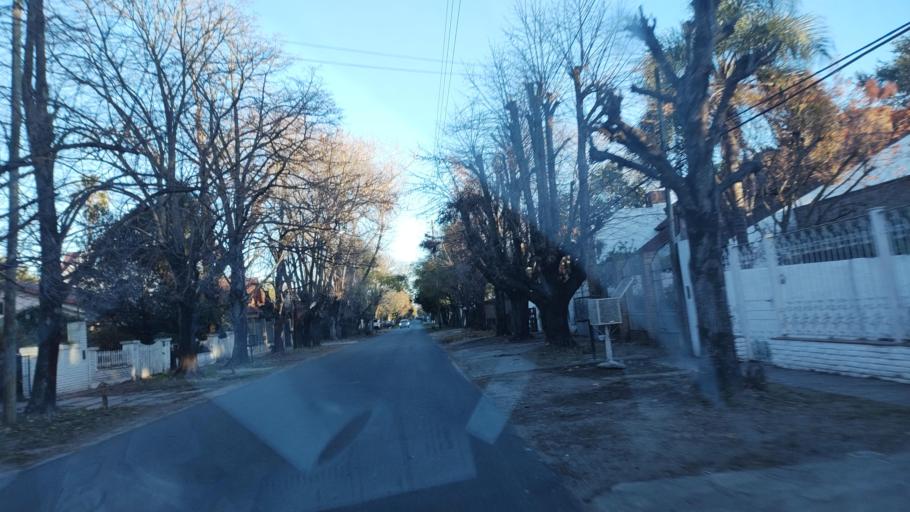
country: AR
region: Buenos Aires
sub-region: Partido de La Plata
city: La Plata
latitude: -34.8889
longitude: -58.0348
